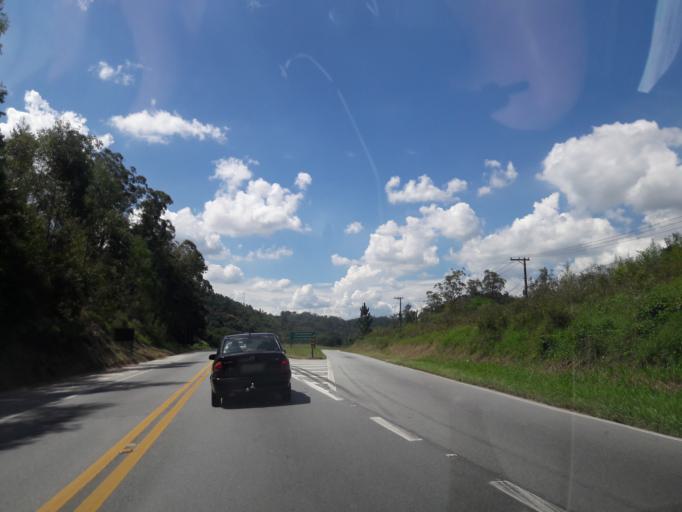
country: BR
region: Sao Paulo
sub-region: Francisco Morato
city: Francisco Morato
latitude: -23.2881
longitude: -46.8004
